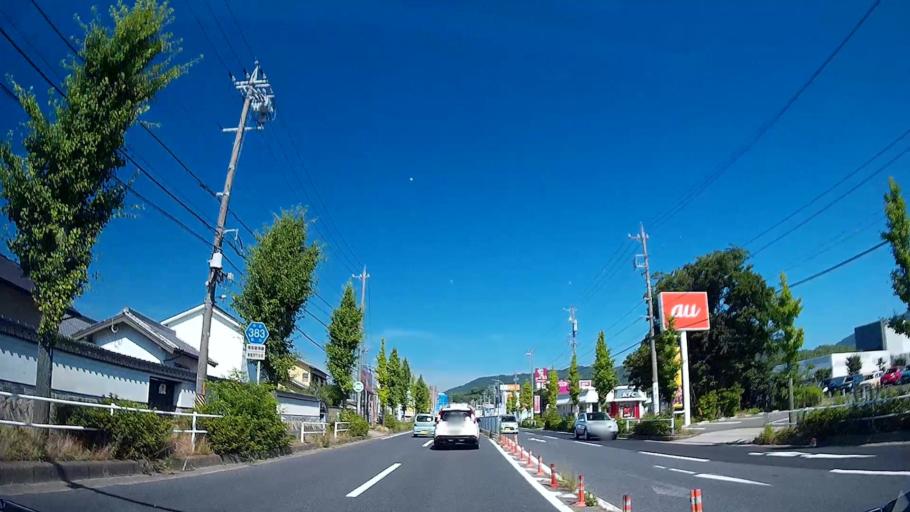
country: JP
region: Aichi
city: Gamagori
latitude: 34.8276
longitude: 137.2110
